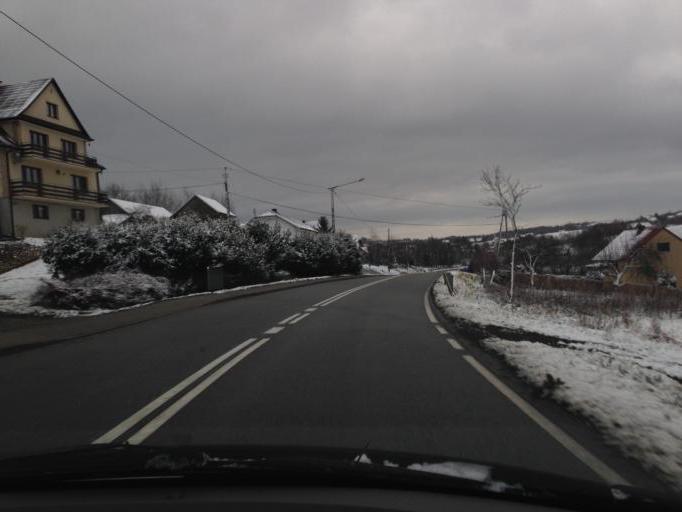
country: PL
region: Lesser Poland Voivodeship
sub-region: Powiat tarnowski
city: Siemiechow
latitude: 49.8527
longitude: 20.9109
